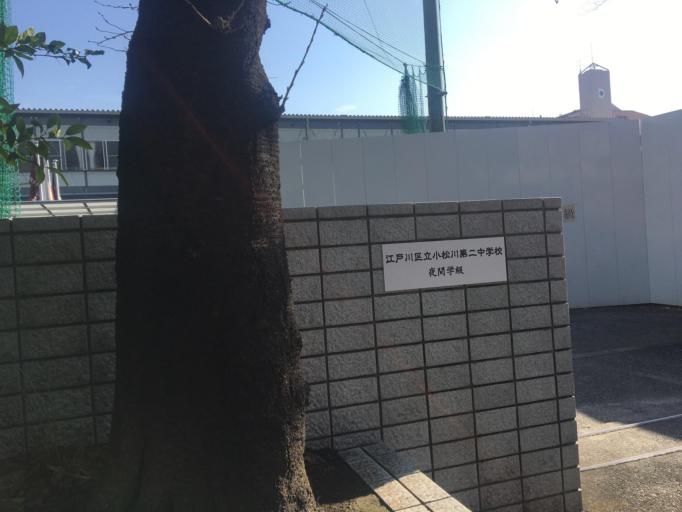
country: JP
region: Tokyo
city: Urayasu
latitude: 35.7029
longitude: 139.8430
